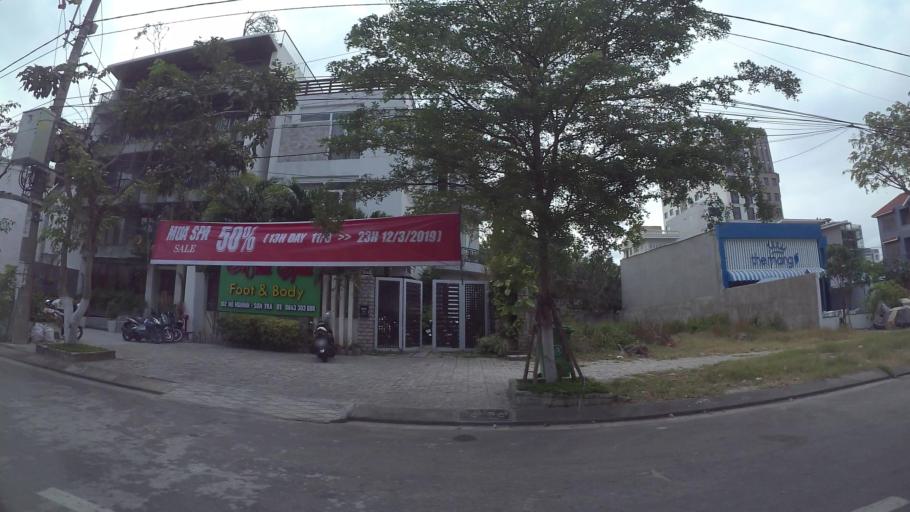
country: VN
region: Da Nang
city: Son Tra
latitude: 16.0747
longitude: 108.2429
